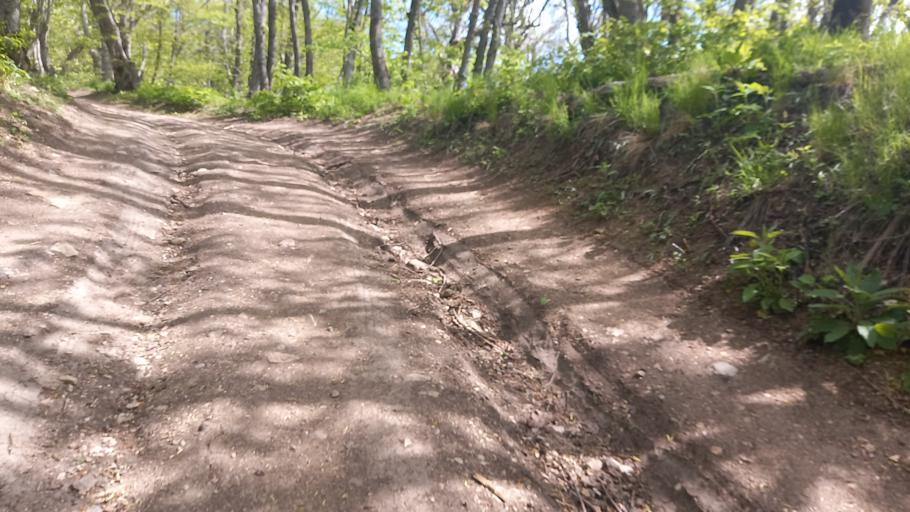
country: RU
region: Stavropol'skiy
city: Pyatigorsk
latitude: 44.0862
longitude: 43.0298
